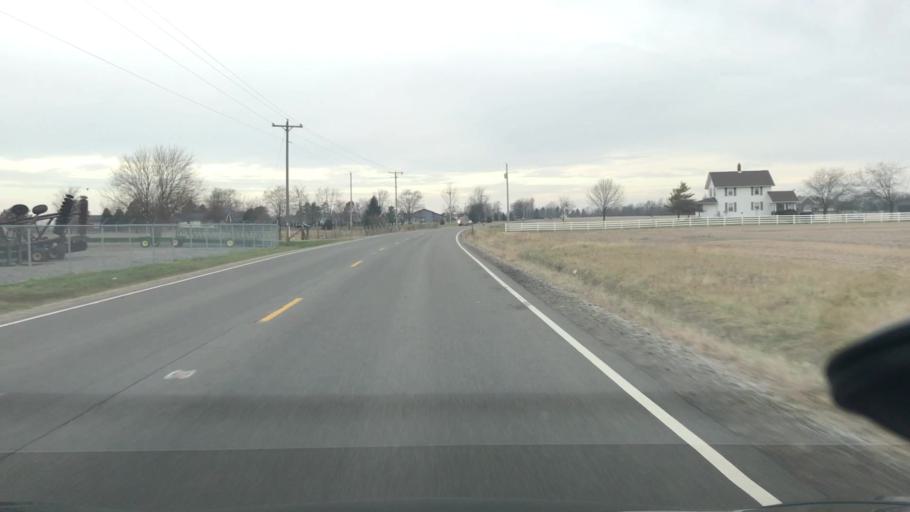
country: US
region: Ohio
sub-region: Madison County
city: Mount Sterling
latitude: 39.7622
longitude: -83.3087
